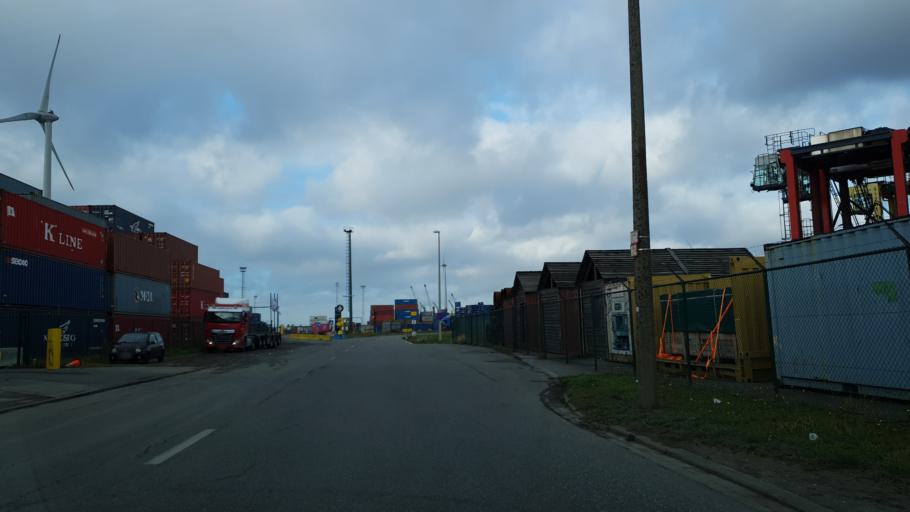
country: BE
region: Flanders
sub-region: Provincie Antwerpen
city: Stabroek
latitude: 51.2754
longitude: 4.3631
